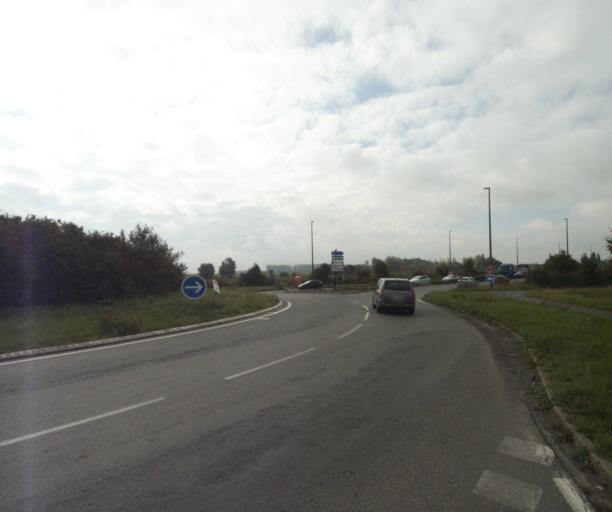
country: FR
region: Nord-Pas-de-Calais
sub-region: Departement du Nord
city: Fournes-en-Weppes
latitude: 50.5791
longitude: 2.8734
